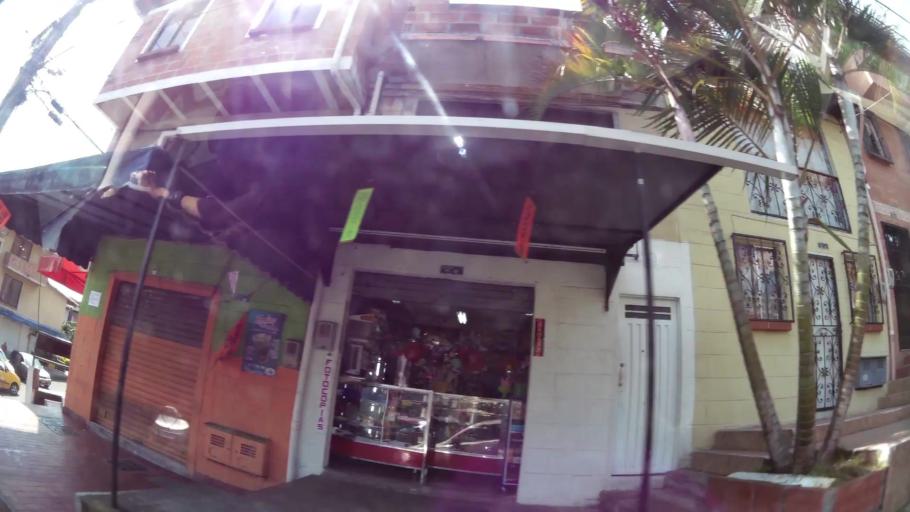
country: CO
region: Antioquia
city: La Estrella
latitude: 6.1754
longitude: -75.6510
